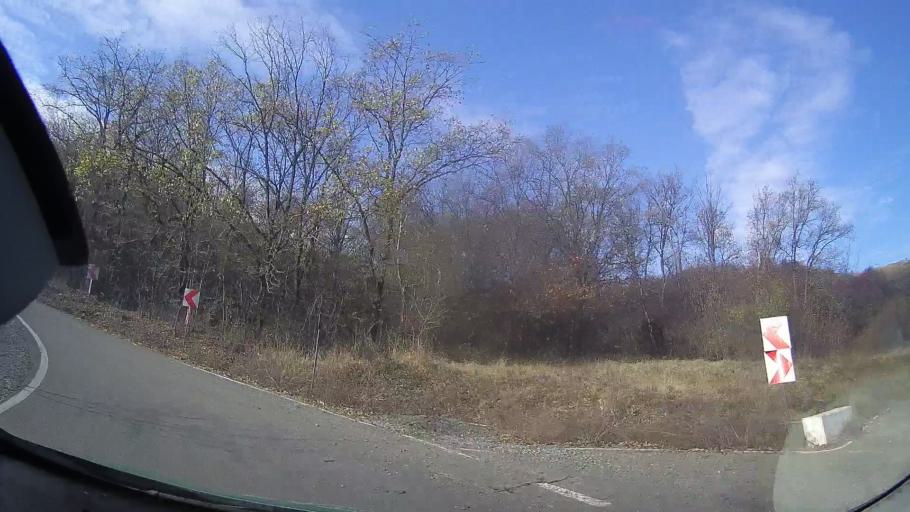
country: RO
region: Mures
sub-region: Comuna Papiu Ilarian
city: Papiu Ilarian
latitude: 46.5589
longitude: 24.1780
